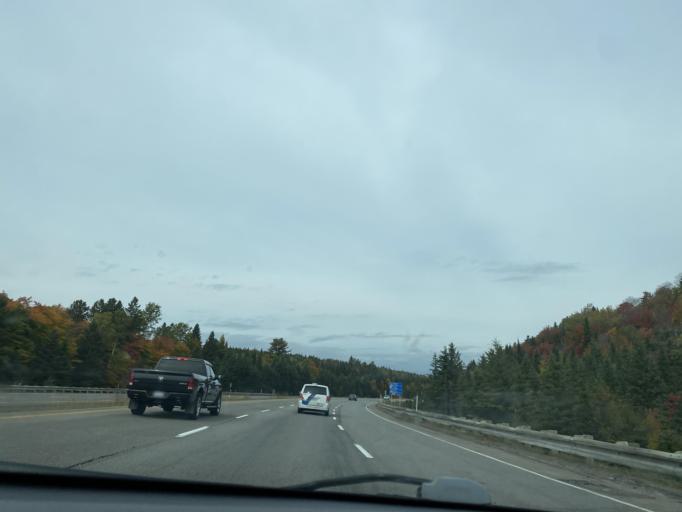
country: CA
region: Quebec
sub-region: Laurentides
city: Val-David
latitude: 46.0142
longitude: -74.2337
